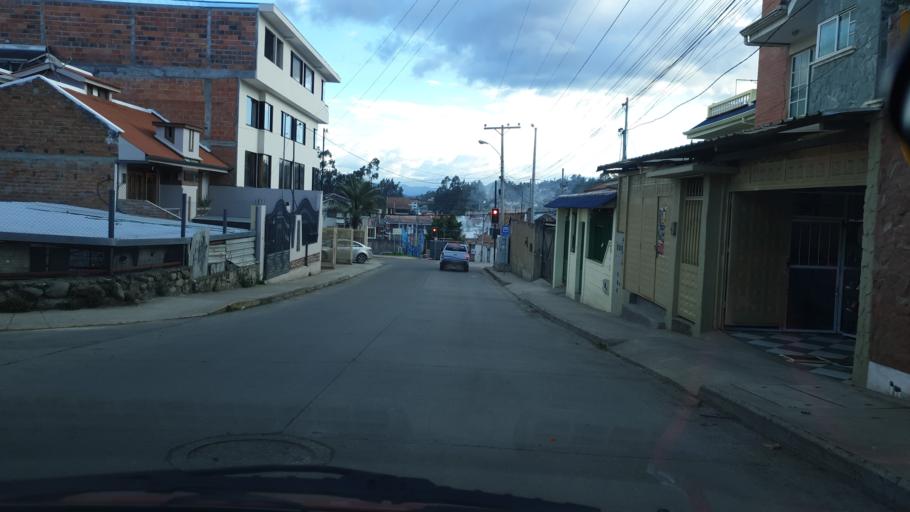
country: EC
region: Azuay
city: Cuenca
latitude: -2.8847
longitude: -79.0430
